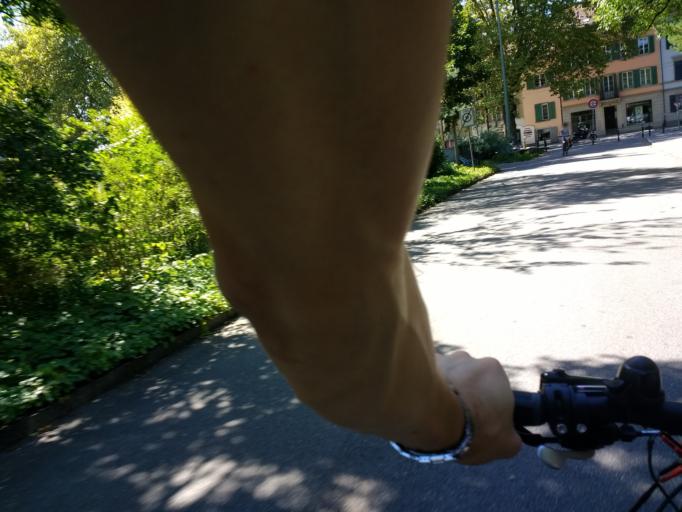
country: CH
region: Zurich
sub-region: Bezirk Winterthur
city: Stadt Winterthur (Kreis 1) / Altstadt
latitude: 47.4993
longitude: 8.7341
